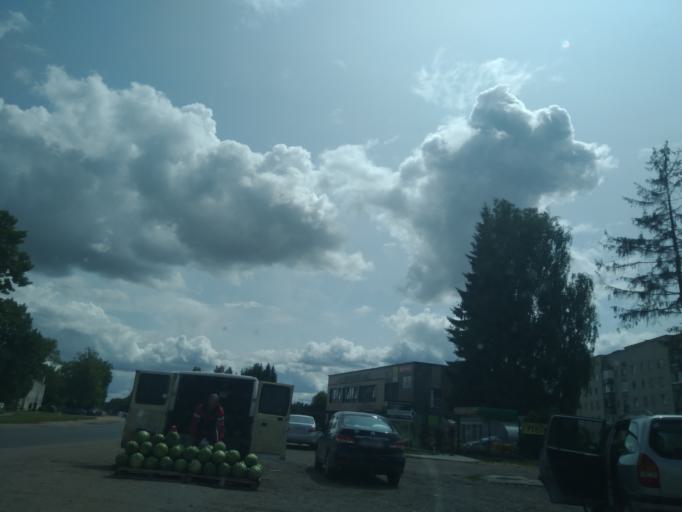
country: BY
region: Minsk
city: Enyerhyetykaw
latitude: 53.5853
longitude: 27.0524
